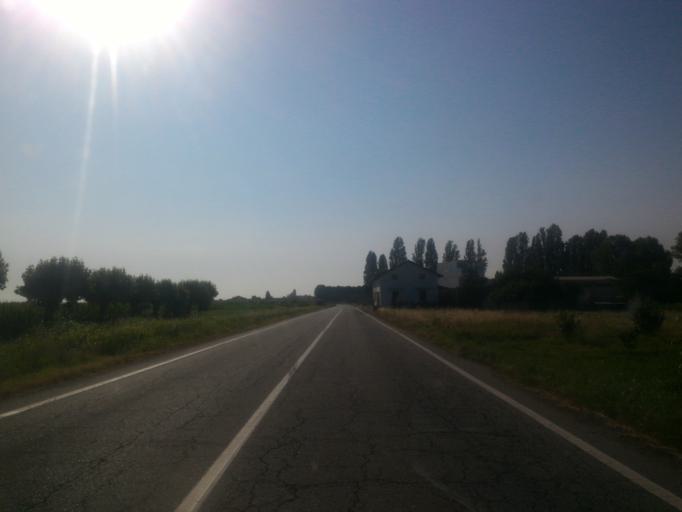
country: IT
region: Piedmont
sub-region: Provincia di Torino
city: Riva
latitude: 44.8777
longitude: 7.3788
